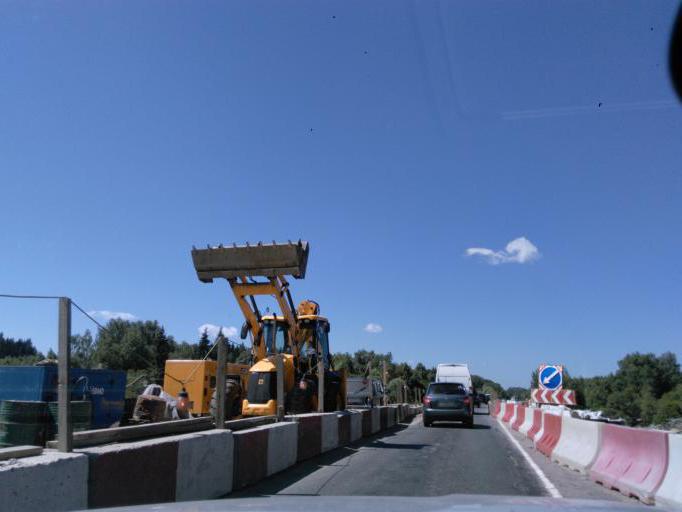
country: RU
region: Moskovskaya
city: Solnechnogorsk
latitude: 56.1438
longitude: 36.9504
